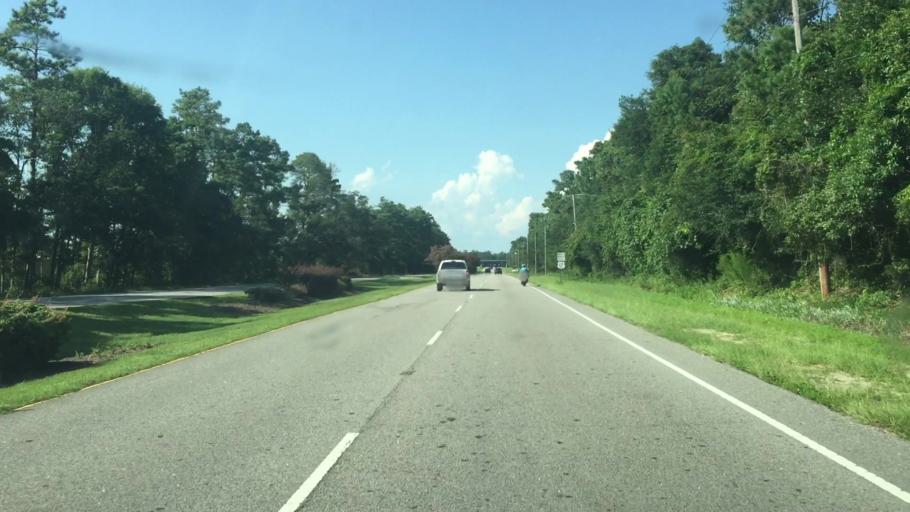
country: US
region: South Carolina
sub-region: Horry County
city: Myrtle Beach
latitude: 33.7589
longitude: -78.8067
